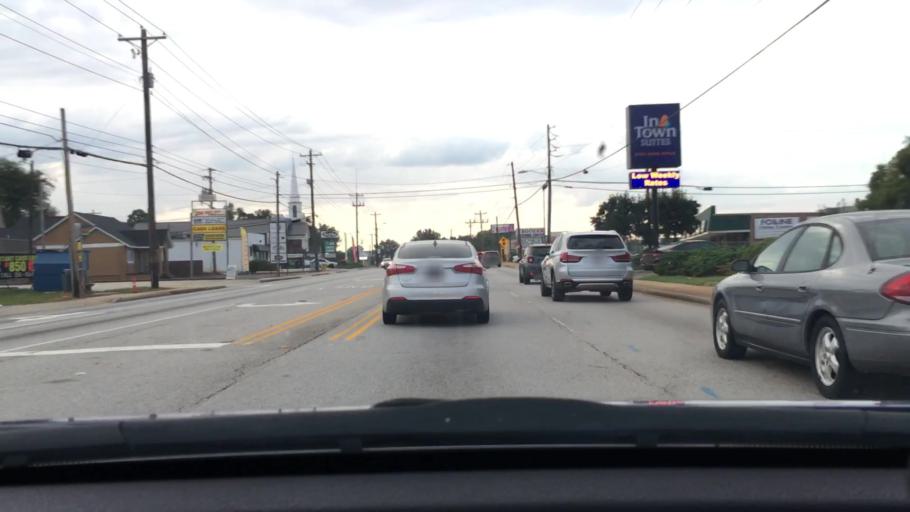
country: US
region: South Carolina
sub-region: Lexington County
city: West Columbia
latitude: 34.0335
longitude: -81.0883
